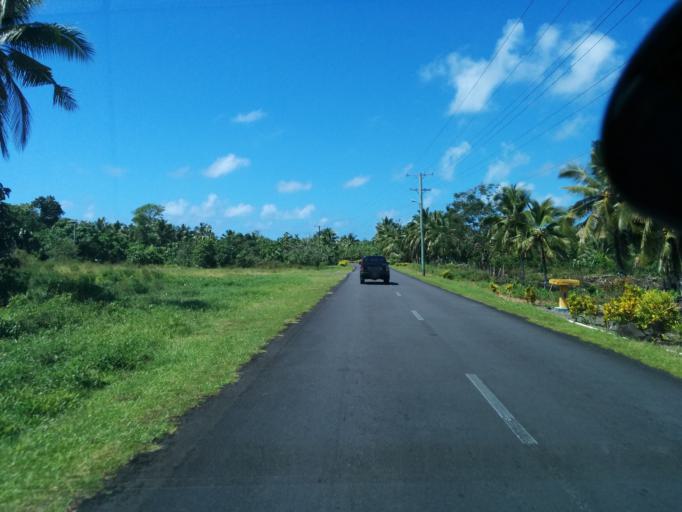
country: WS
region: Fa`asaleleaga
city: Safotulafai
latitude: -13.5781
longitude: -172.2231
